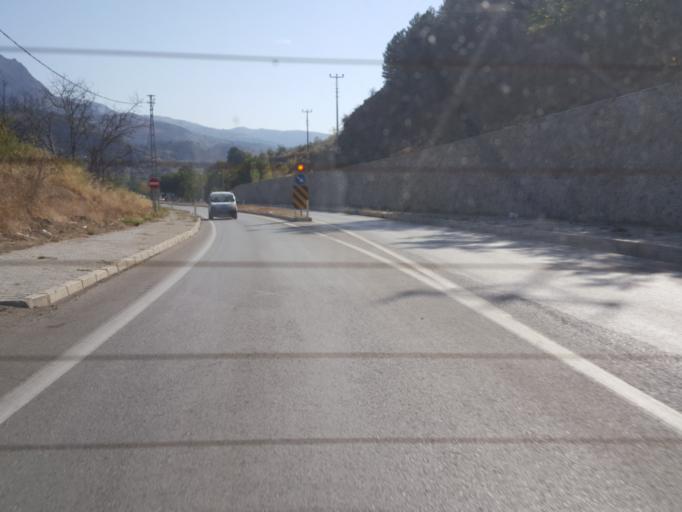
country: TR
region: Corum
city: Iskilip
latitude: 40.7376
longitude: 34.4532
